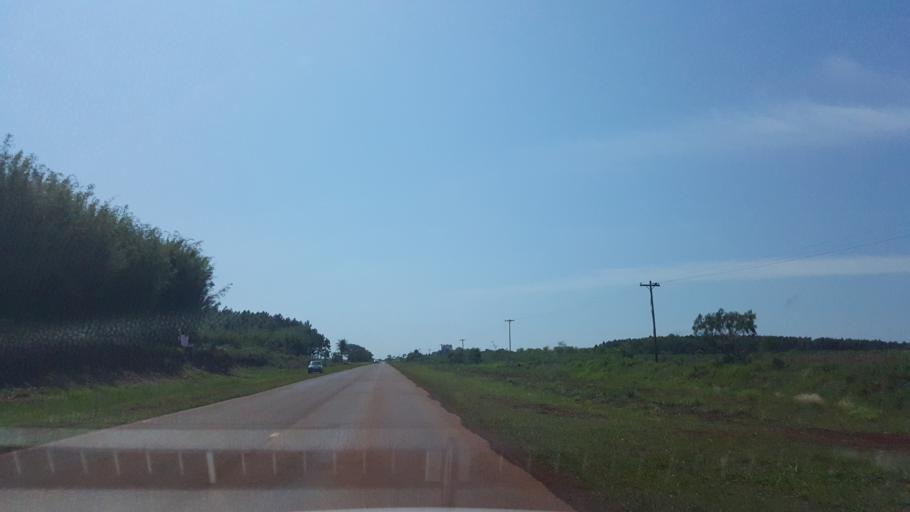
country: AR
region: Corrientes
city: San Carlos
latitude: -27.7516
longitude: -55.8849
